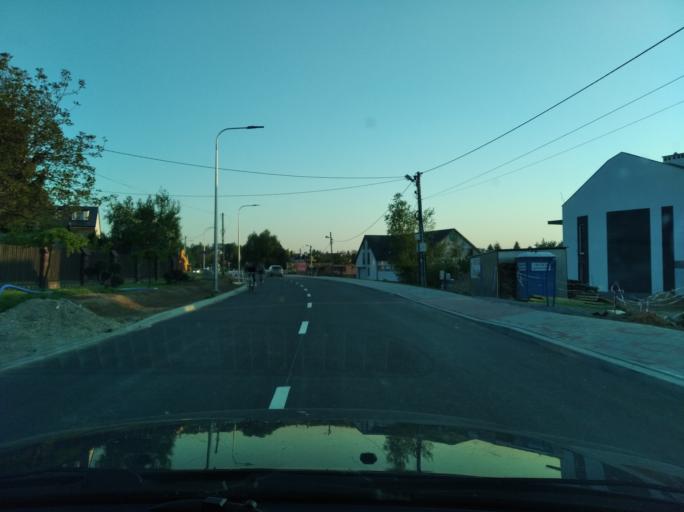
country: PL
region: Subcarpathian Voivodeship
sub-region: Powiat rzeszowski
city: Tyczyn
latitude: 50.0112
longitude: 22.0376
